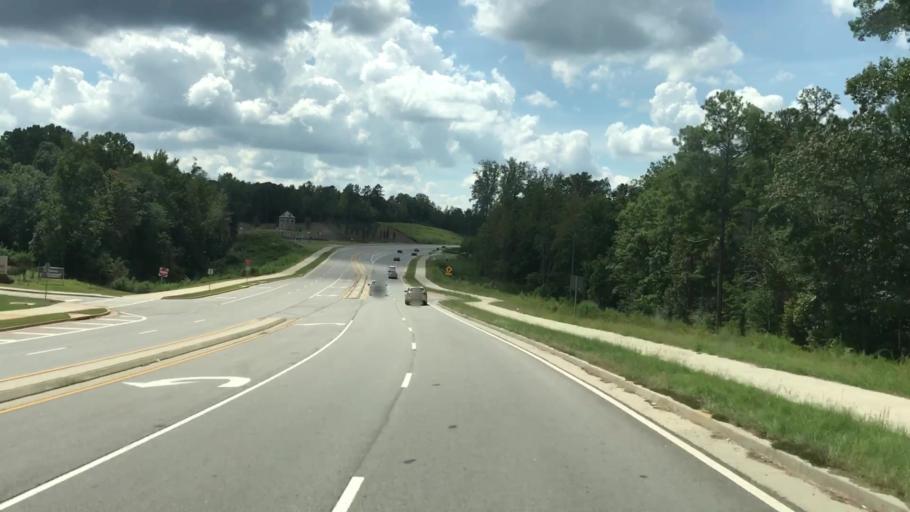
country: US
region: Georgia
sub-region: Jackson County
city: Braselton
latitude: 34.1129
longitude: -83.8576
